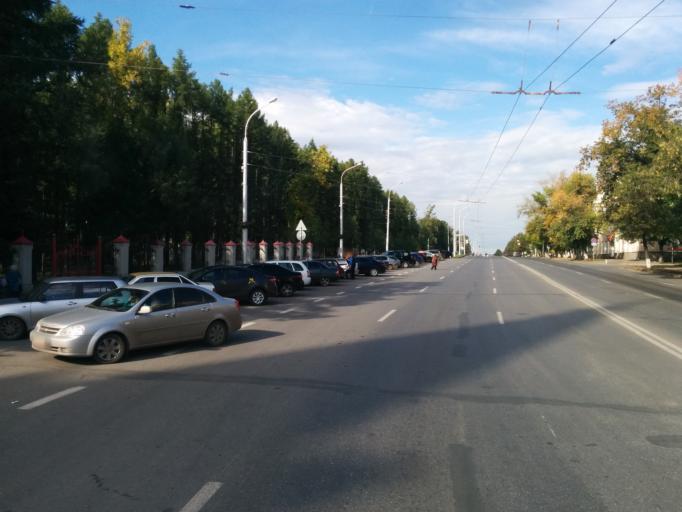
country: RU
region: Bashkortostan
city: Ufa
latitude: 54.8201
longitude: 56.0570
